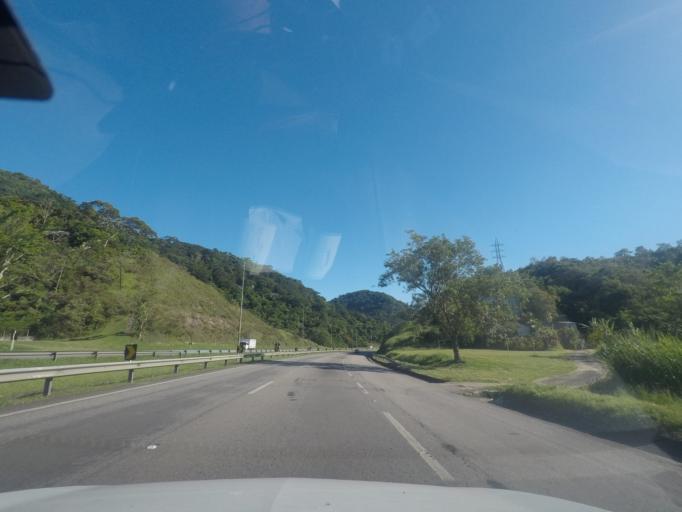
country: BR
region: Rio de Janeiro
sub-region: Guapimirim
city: Guapimirim
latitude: -22.5760
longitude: -43.0096
